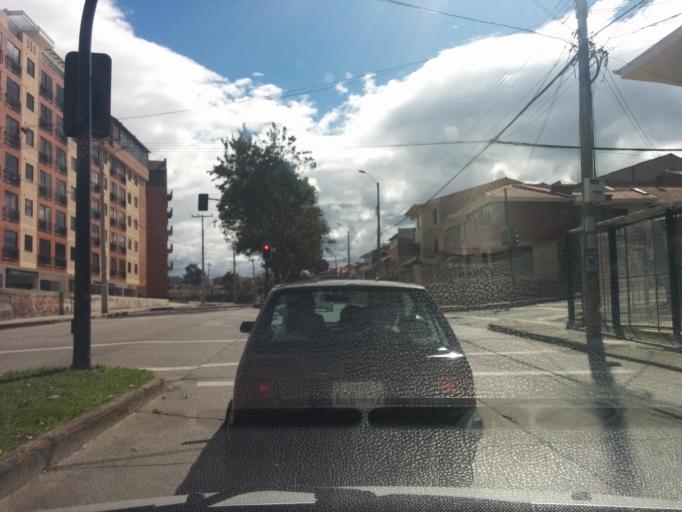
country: EC
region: Azuay
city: Cuenca
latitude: -2.9037
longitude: -78.9899
